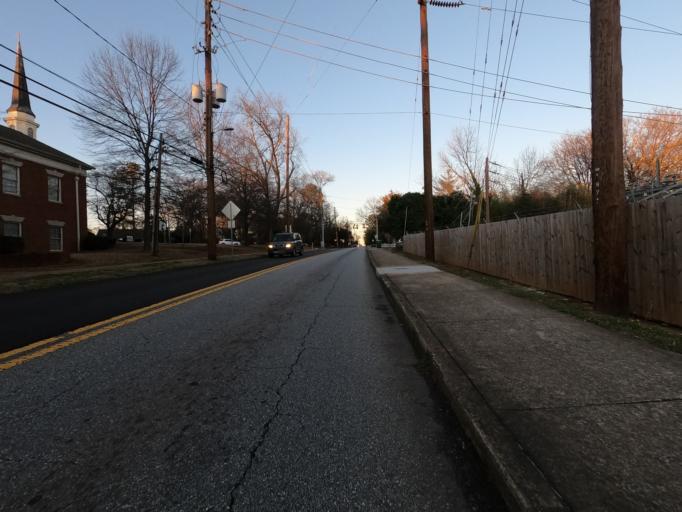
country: US
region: Georgia
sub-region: Clarke County
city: Athens
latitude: 33.9318
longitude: -83.3926
